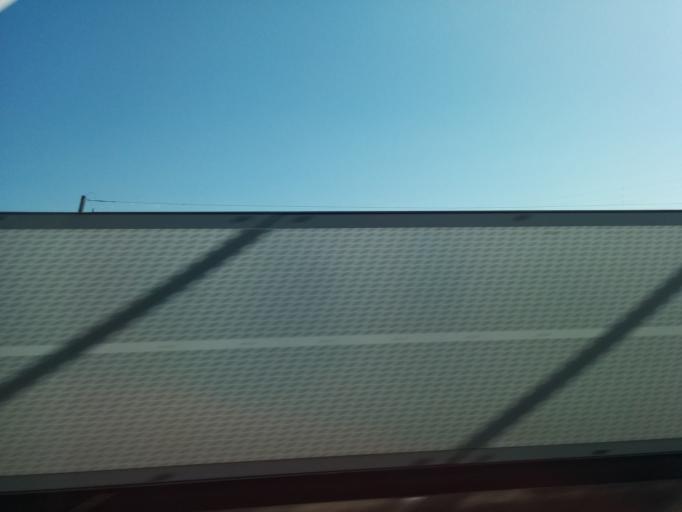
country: JP
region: Shiga Prefecture
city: Hikone
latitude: 35.1975
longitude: 136.2309
